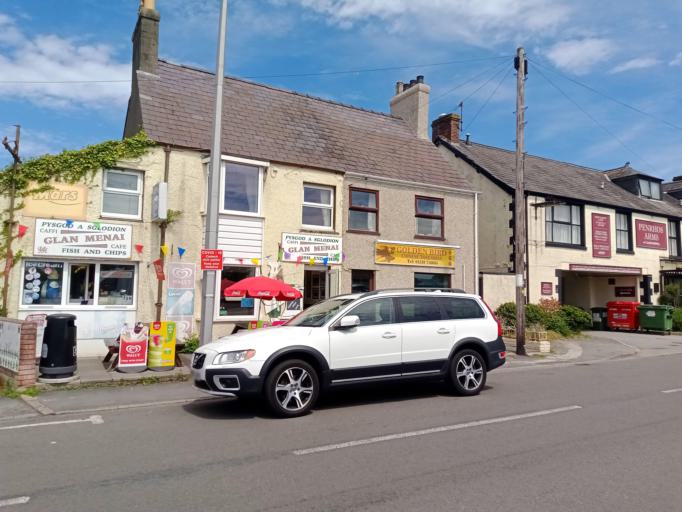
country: GB
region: Wales
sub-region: Anglesey
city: Llanfairpwllgwyngyll
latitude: 53.2214
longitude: -4.2098
